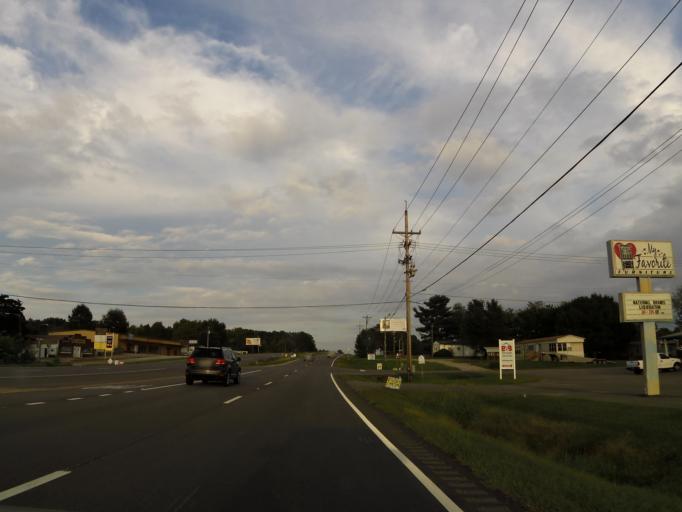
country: US
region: Alabama
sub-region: Madison County
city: Madison
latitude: 34.7489
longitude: -86.7970
